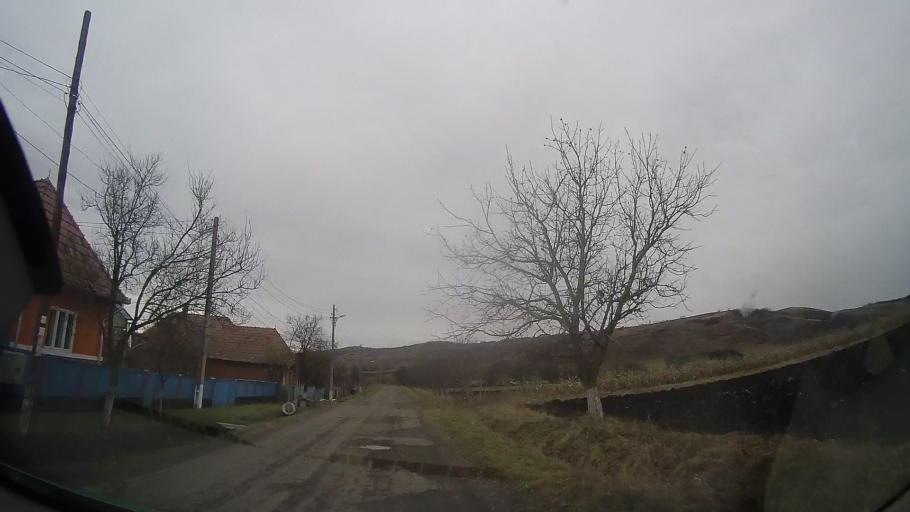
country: RO
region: Mures
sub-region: Comuna Bala
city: Bala
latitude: 46.7060
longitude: 24.4990
